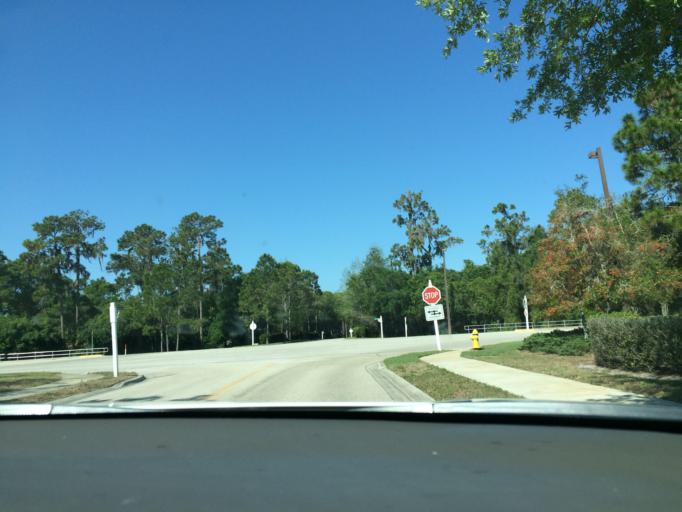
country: US
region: Florida
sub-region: Sarasota County
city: The Meadows
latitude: 27.4306
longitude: -82.4277
